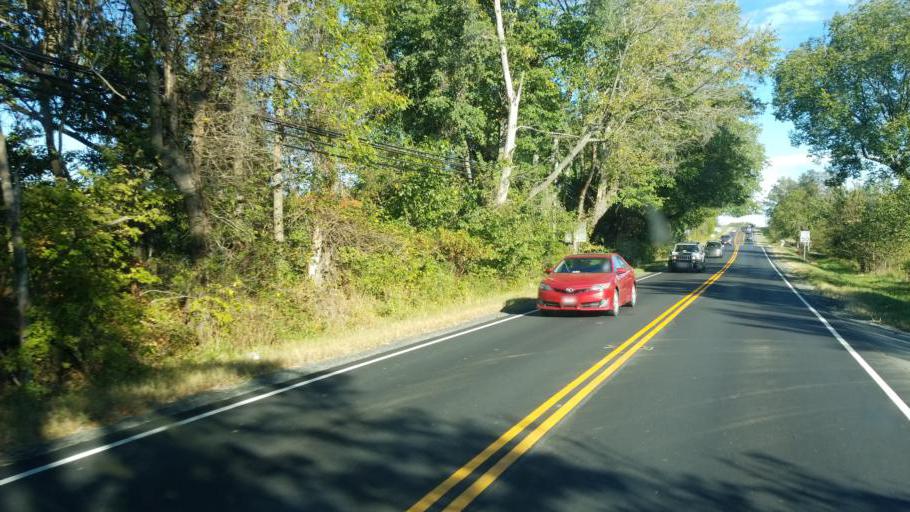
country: US
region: Virginia
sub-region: Loudoun County
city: Brambleton
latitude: 38.9630
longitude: -77.6063
